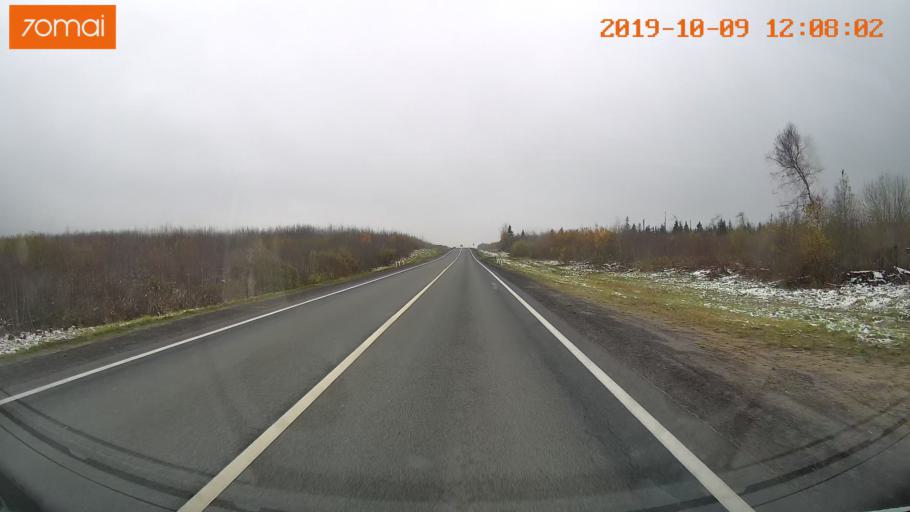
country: RU
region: Jaroslavl
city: Prechistoye
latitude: 58.5918
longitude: 40.3455
